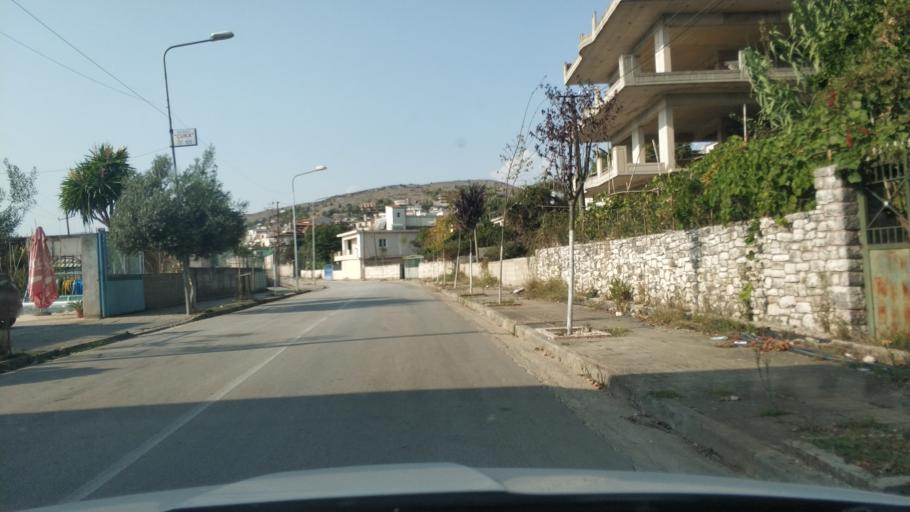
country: AL
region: Vlore
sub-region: Rrethi i Sarandes
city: Sarande
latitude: 39.8445
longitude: 20.0341
